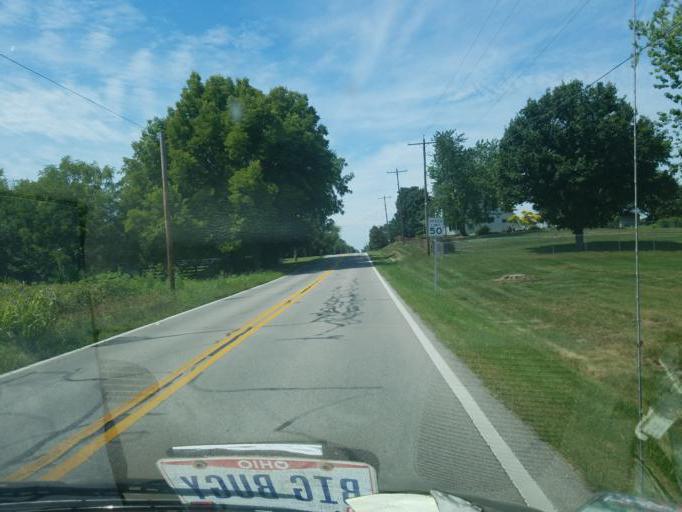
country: US
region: Ohio
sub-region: Franklin County
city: Grove City
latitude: 39.8750
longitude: -83.1679
